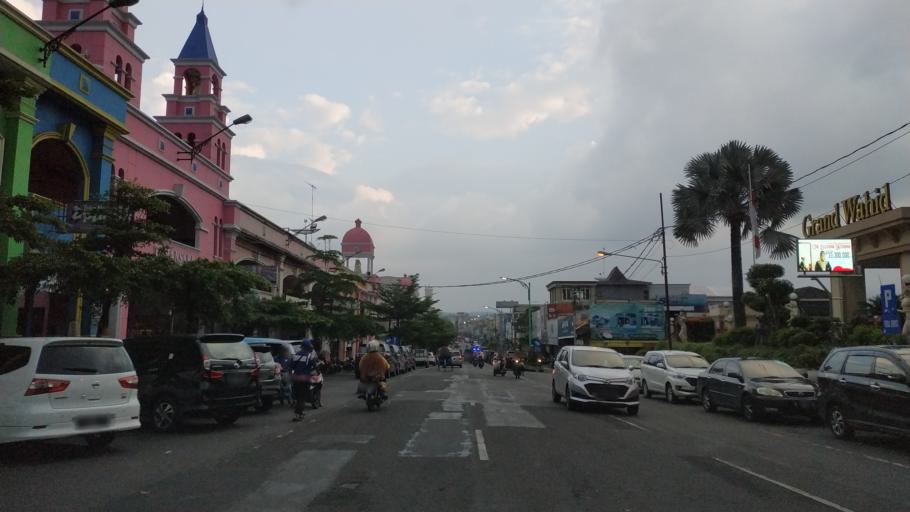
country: ID
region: Central Java
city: Salatiga
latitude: -7.3258
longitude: 110.5048
